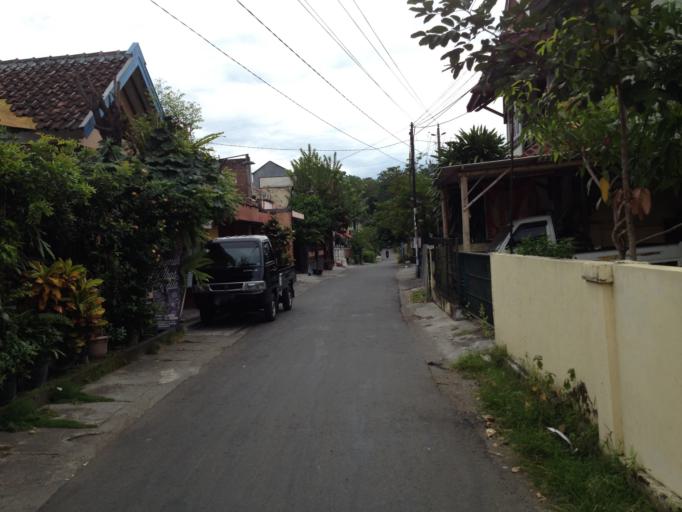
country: ID
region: Daerah Istimewa Yogyakarta
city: Yogyakarta
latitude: -7.8073
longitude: 110.4000
